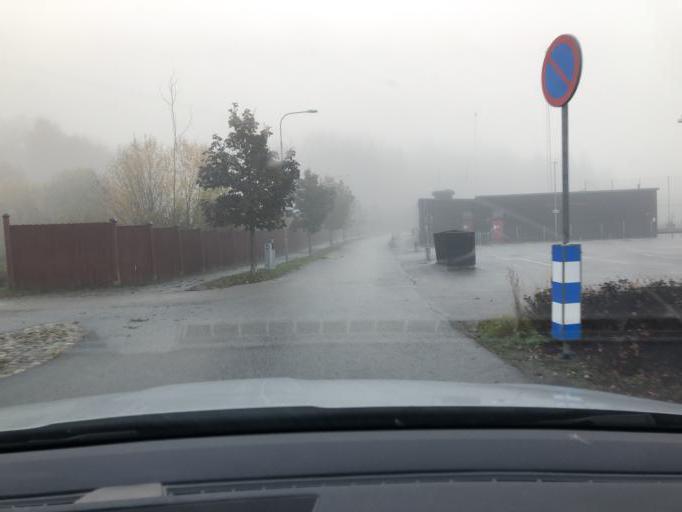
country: SE
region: Stockholm
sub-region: Huddinge Kommun
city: Segeltorp
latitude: 59.2679
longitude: 17.9308
